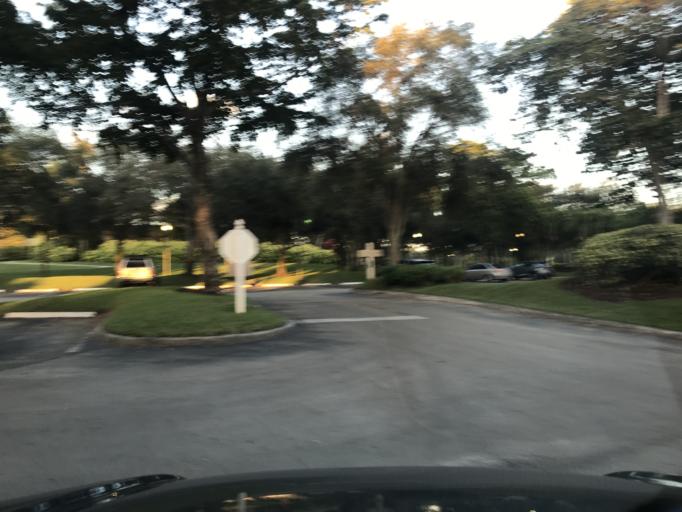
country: US
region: Florida
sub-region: Broward County
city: Pine Island Ridge
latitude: 26.1116
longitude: -80.2727
